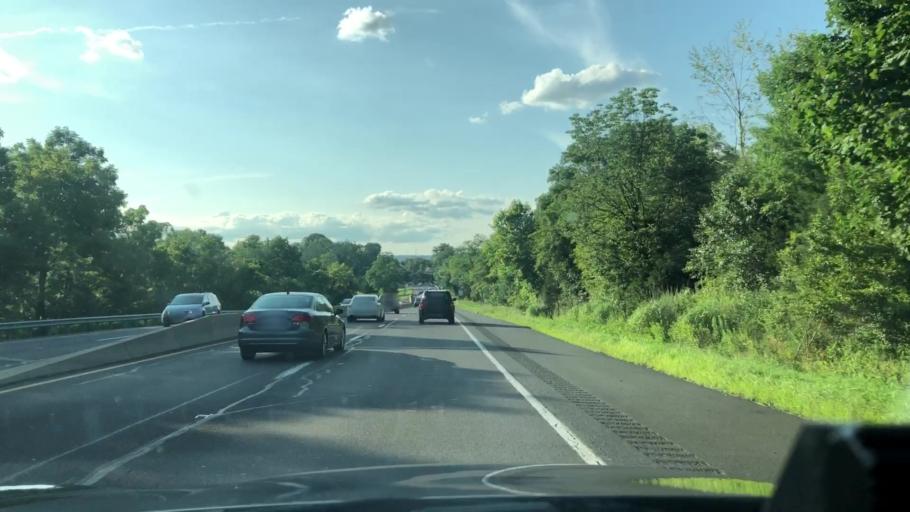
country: US
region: Pennsylvania
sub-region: Lehigh County
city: Coopersburg
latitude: 40.5247
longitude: -75.3891
